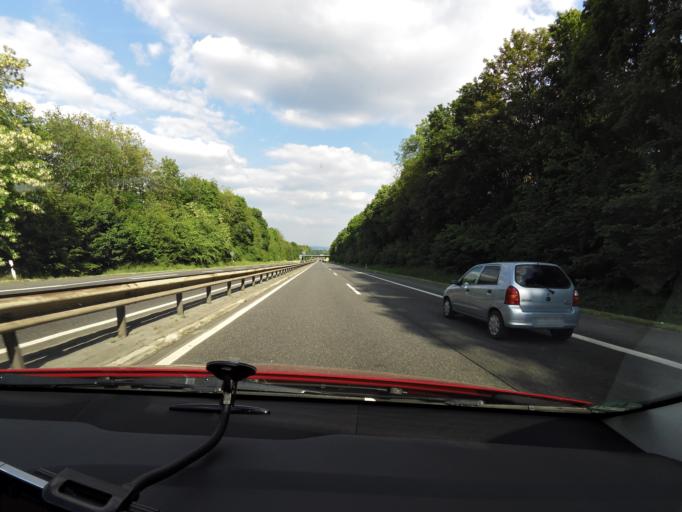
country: DE
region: Rheinland-Pfalz
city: Andernach
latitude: 50.4221
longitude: 7.4005
